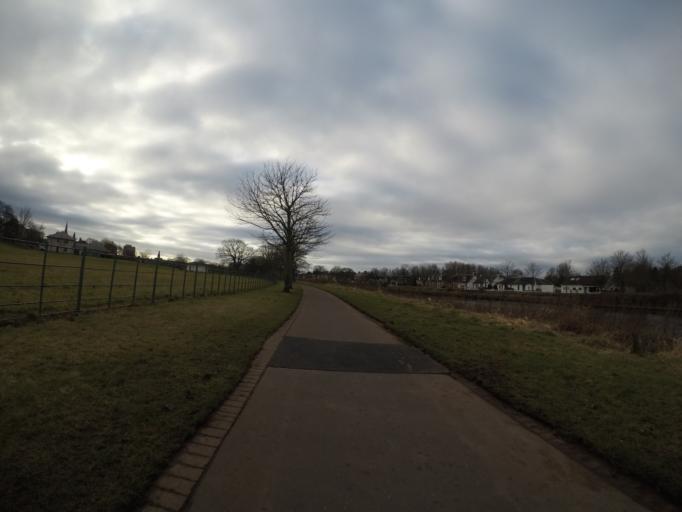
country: GB
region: Scotland
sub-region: North Ayrshire
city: Irvine
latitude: 55.6182
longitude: -4.6736
